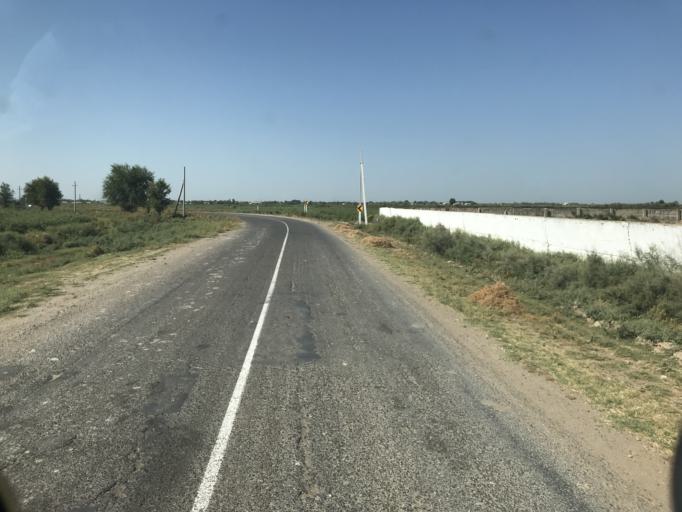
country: KZ
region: Ongtustik Qazaqstan
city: Myrzakent
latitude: 40.6834
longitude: 68.5578
